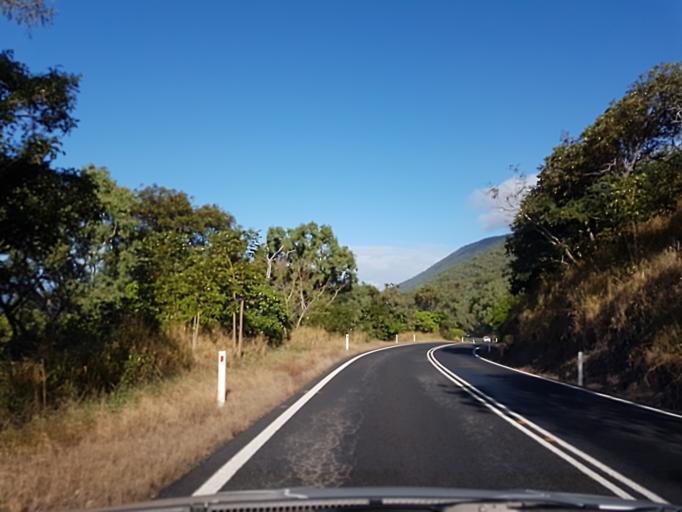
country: AU
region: Queensland
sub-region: Cairns
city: Palm Cove
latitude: -16.7078
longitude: 145.6303
